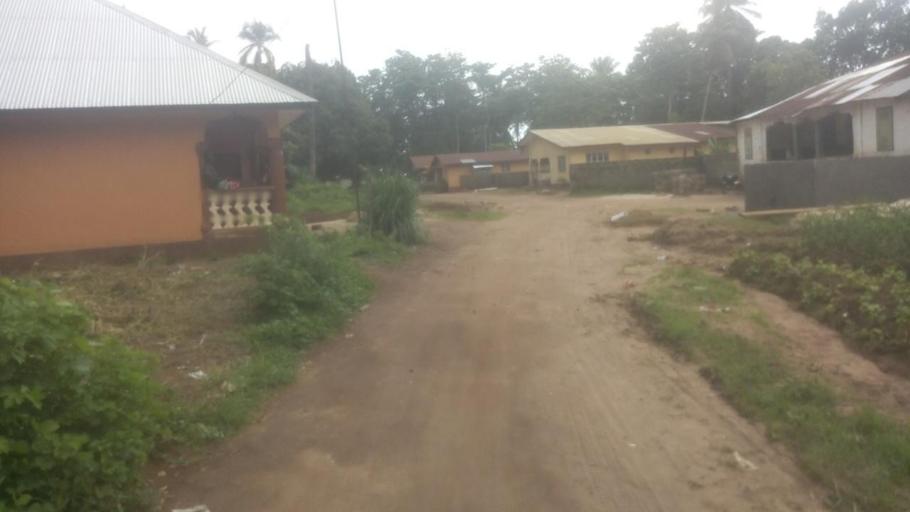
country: SL
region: Northern Province
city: Tintafor
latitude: 8.6425
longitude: -13.2246
